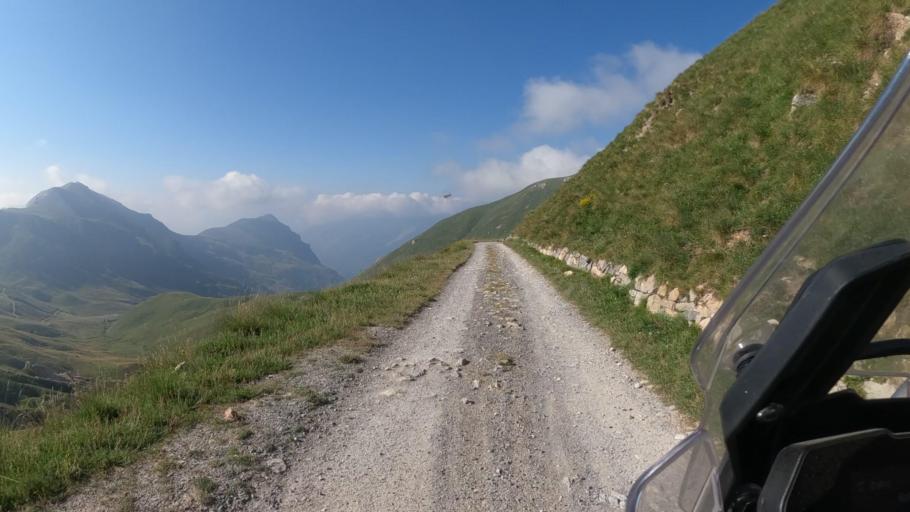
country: IT
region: Piedmont
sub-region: Provincia di Cuneo
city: Pietraporzio
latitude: 44.3861
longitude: 7.0653
